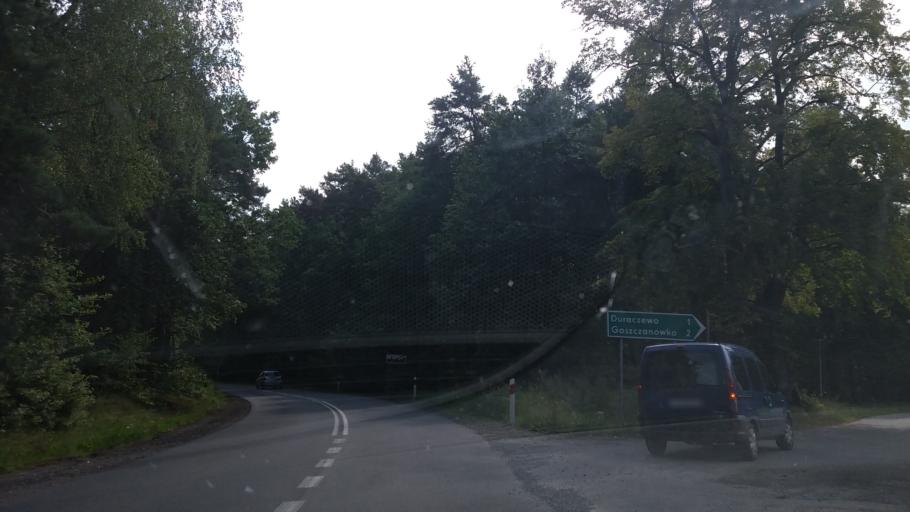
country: PL
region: Lubusz
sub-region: Powiat strzelecko-drezdenecki
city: Stare Kurowo
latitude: 52.7575
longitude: 15.6427
